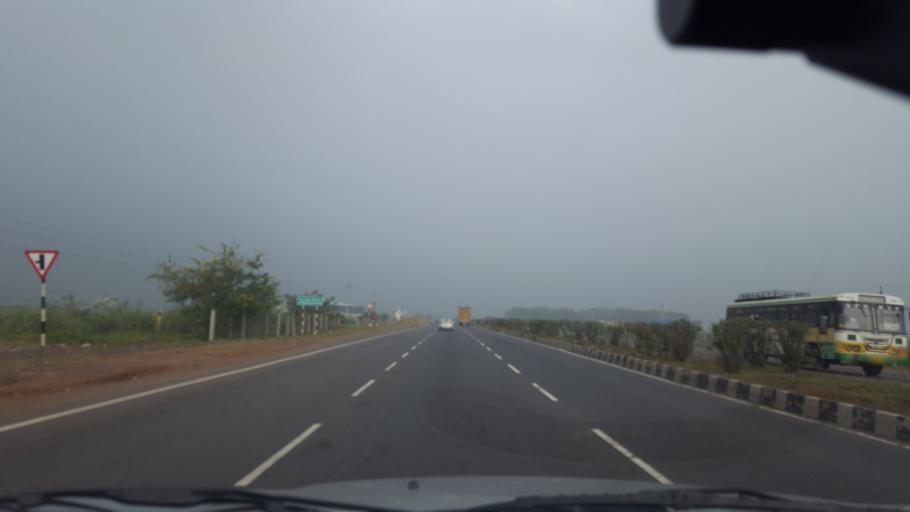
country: IN
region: Andhra Pradesh
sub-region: Prakasam
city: Ongole
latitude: 15.5746
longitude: 80.0437
